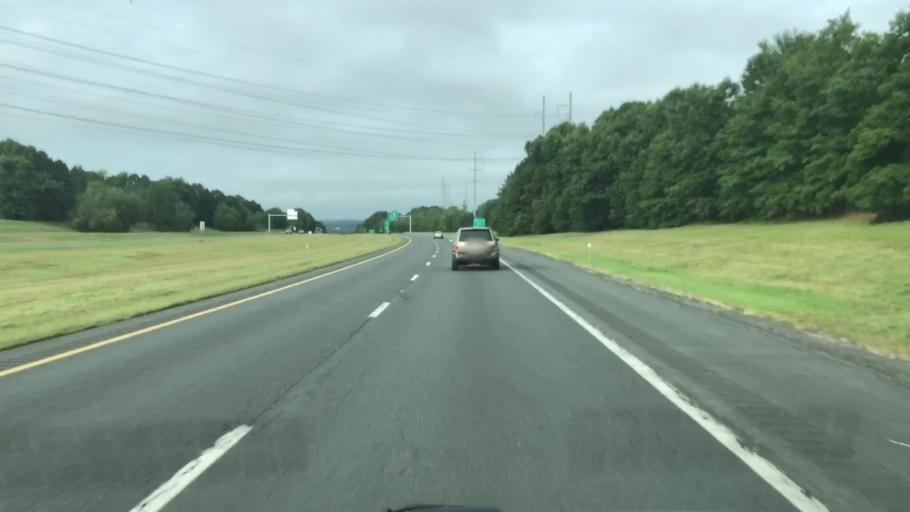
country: US
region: Massachusetts
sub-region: Hampden County
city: North Chicopee
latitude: 42.1661
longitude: -72.5995
